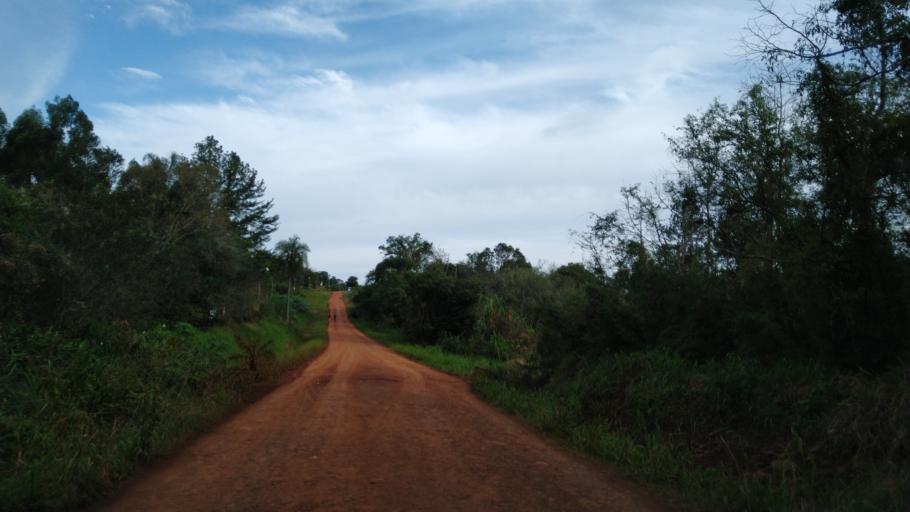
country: AR
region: Misiones
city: Capiovi
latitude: -26.9377
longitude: -55.0967
